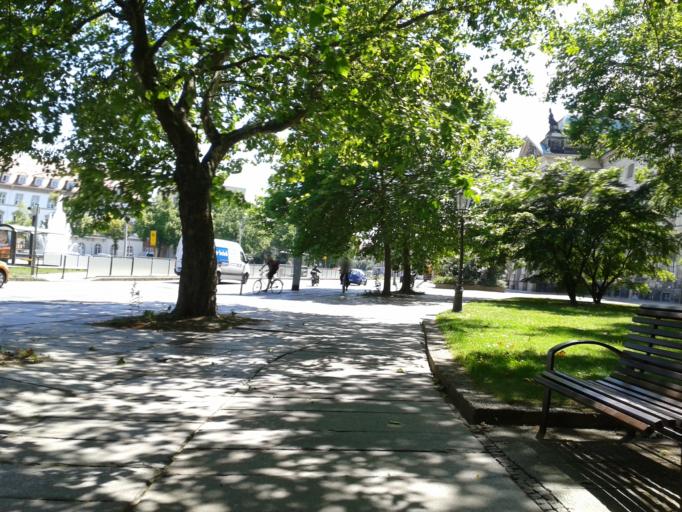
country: DE
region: Saxony
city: Dresden
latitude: 51.0609
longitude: 13.7376
